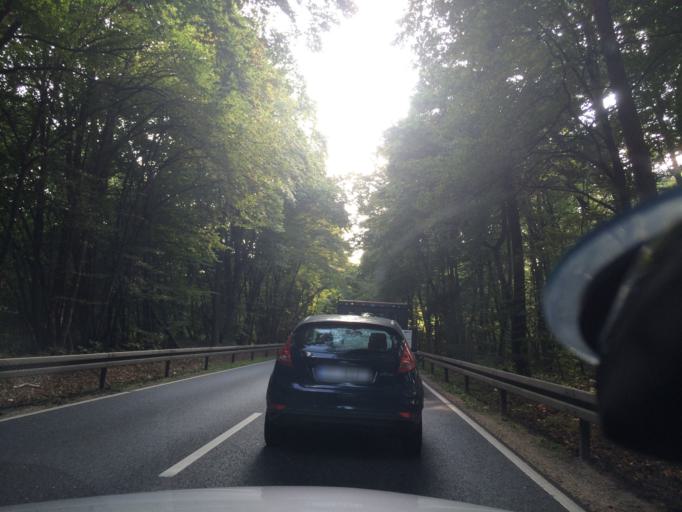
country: DE
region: Hesse
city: Morfelden-Walldorf
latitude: 50.0138
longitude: 8.6014
